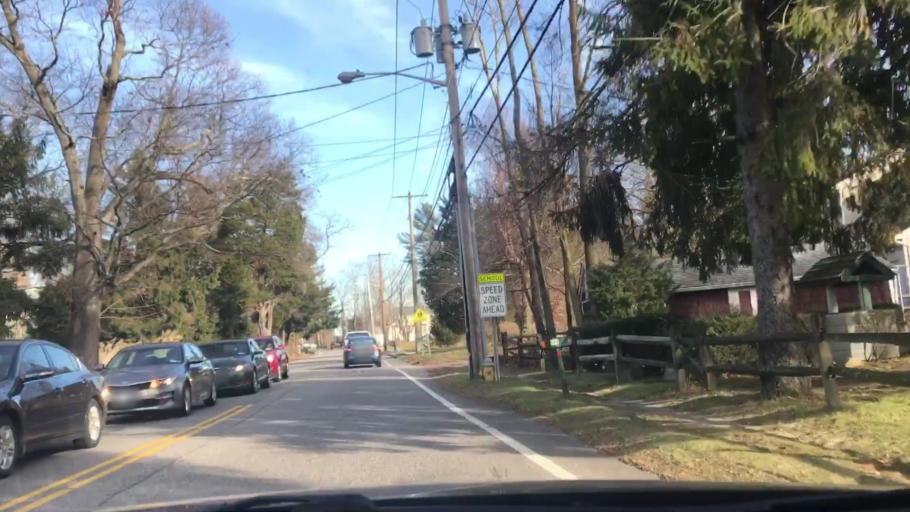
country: US
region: New York
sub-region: Suffolk County
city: Lake Grove
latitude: 40.8375
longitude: -73.1100
